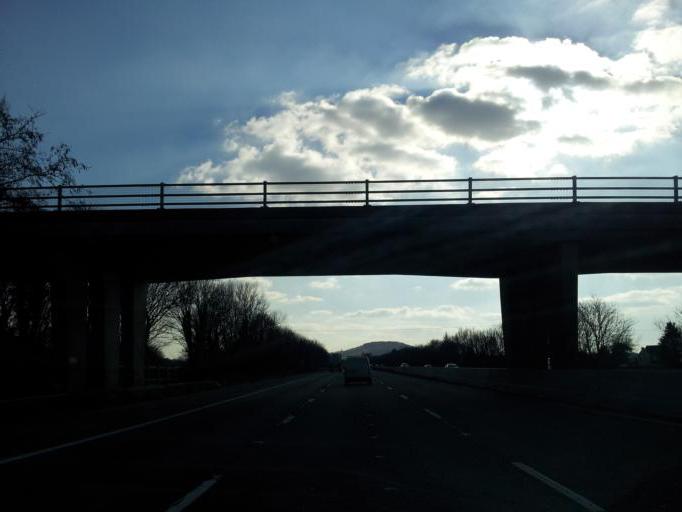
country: GB
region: England
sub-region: North Somerset
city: Bleadon
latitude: 51.2762
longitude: -2.9143
